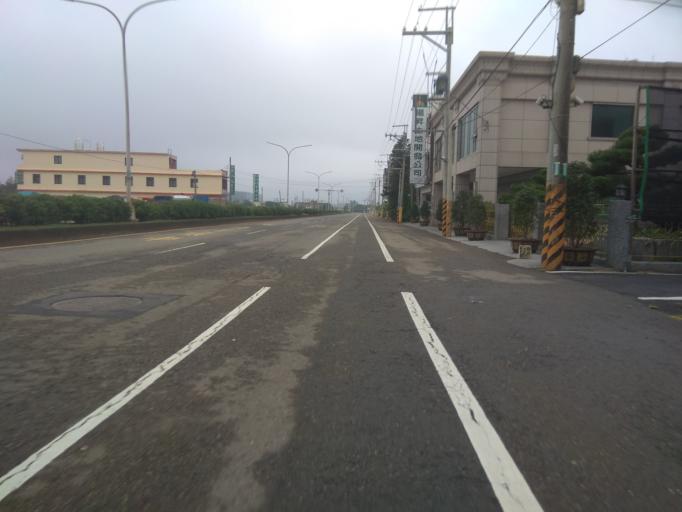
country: TW
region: Taiwan
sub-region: Hsinchu
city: Zhubei
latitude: 25.0284
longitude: 121.0782
